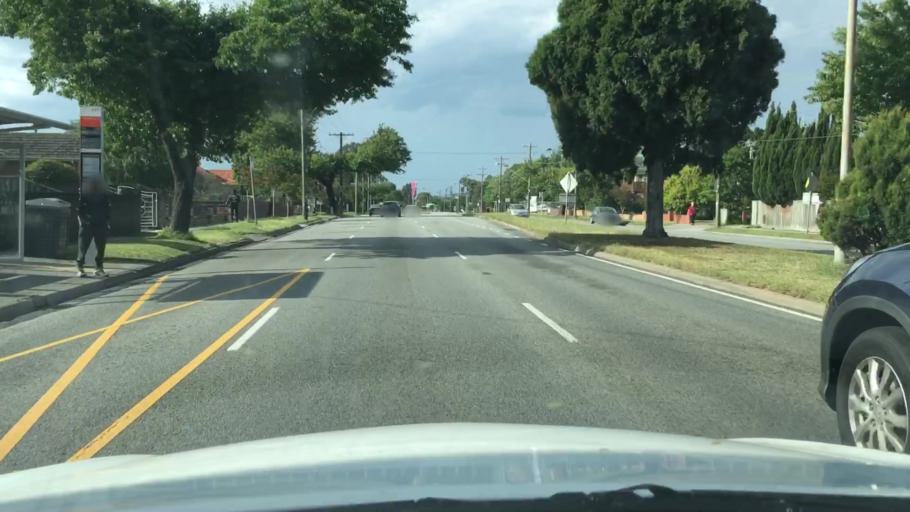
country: AU
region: Victoria
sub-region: Greater Dandenong
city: Springvale South
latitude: -37.9584
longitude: 145.1511
